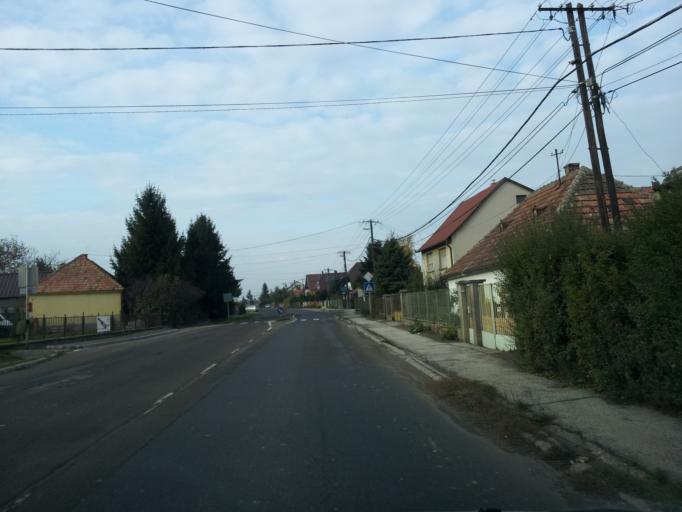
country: HU
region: Gyor-Moson-Sopron
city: Pannonhalma
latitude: 47.5208
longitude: 17.7499
